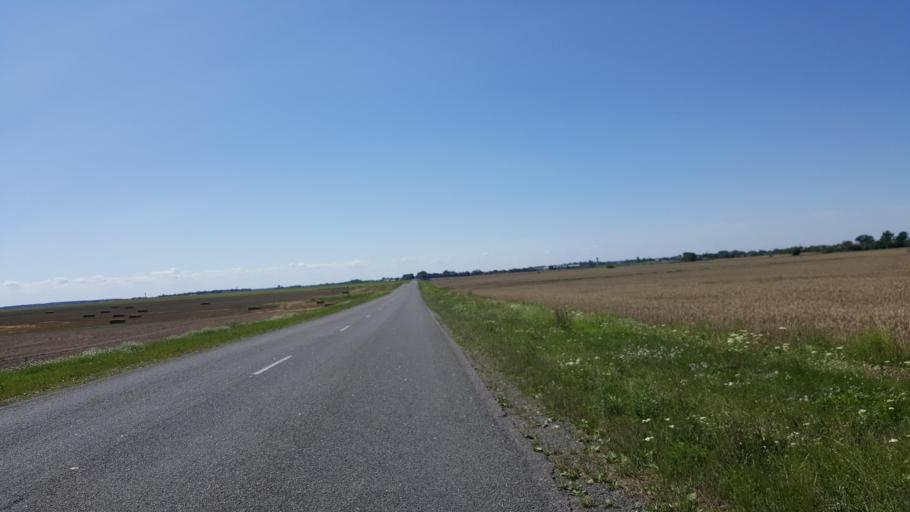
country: BY
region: Brest
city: Charnawchytsy
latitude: 52.2059
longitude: 23.7989
